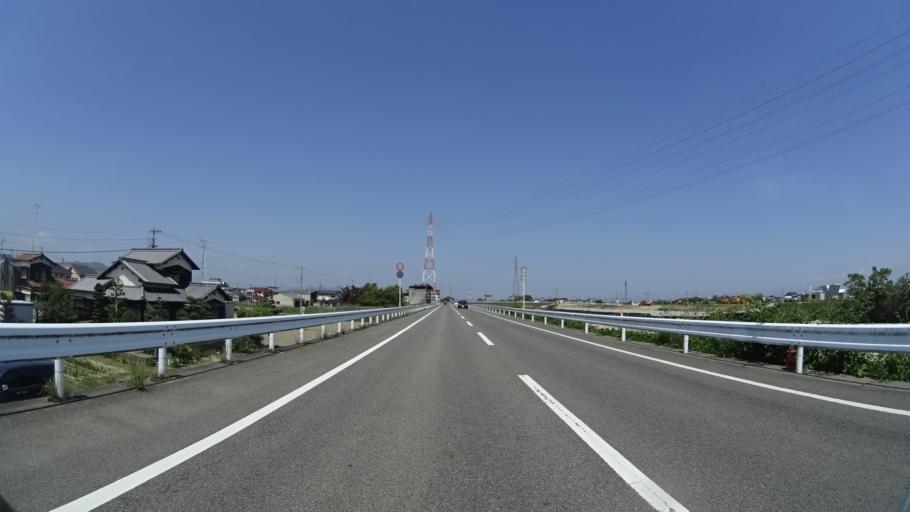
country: JP
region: Ehime
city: Hojo
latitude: 34.0365
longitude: 132.9740
